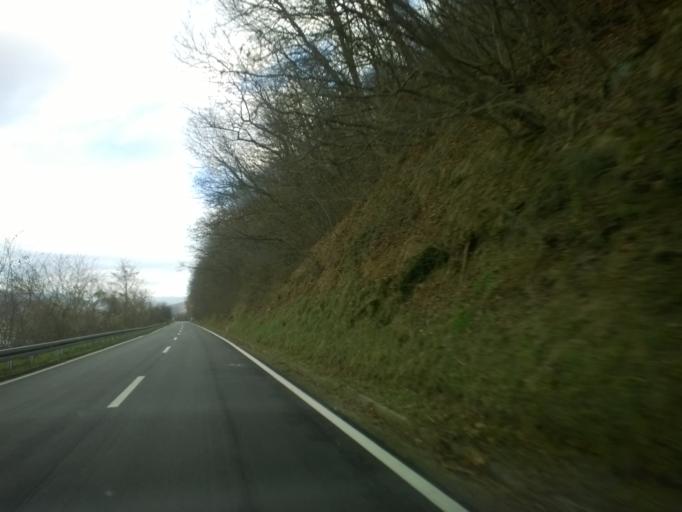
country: RO
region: Caras-Severin
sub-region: Comuna Berzasca
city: Liubcova
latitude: 44.6447
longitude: 21.8758
